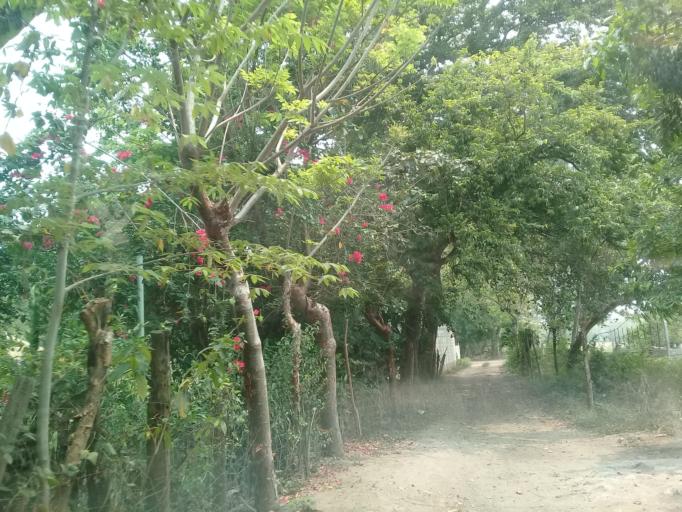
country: MX
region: Veracruz
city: Jamapa
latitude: 18.9514
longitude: -96.2051
